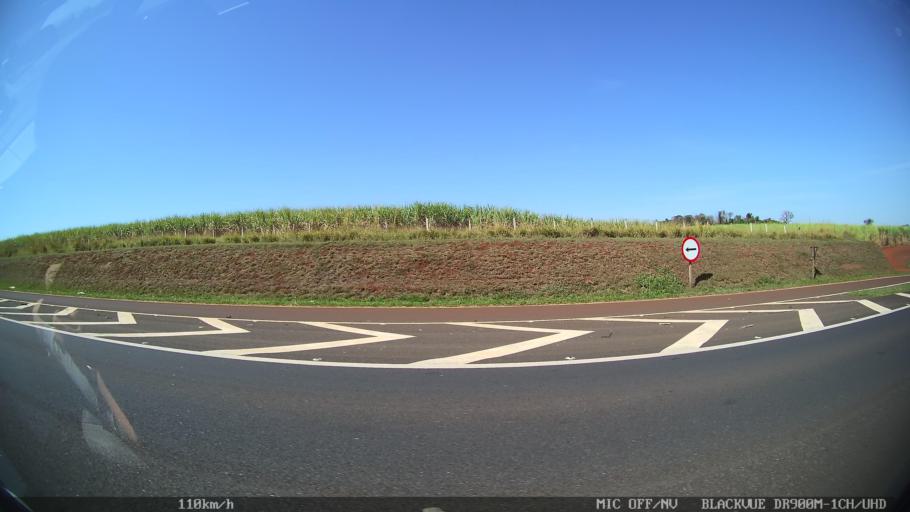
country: BR
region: Sao Paulo
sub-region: Batatais
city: Batatais
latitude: -20.7848
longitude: -47.5541
